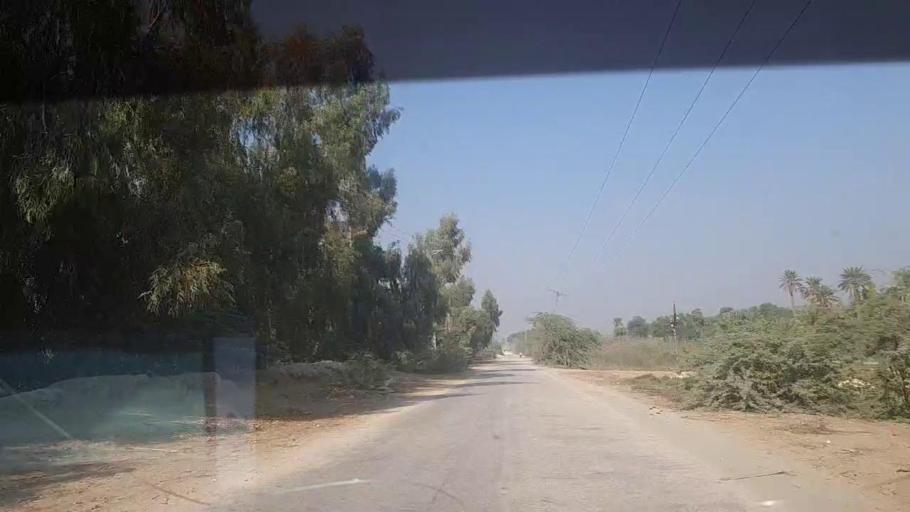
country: PK
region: Sindh
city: Kot Diji
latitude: 27.3544
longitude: 68.7111
